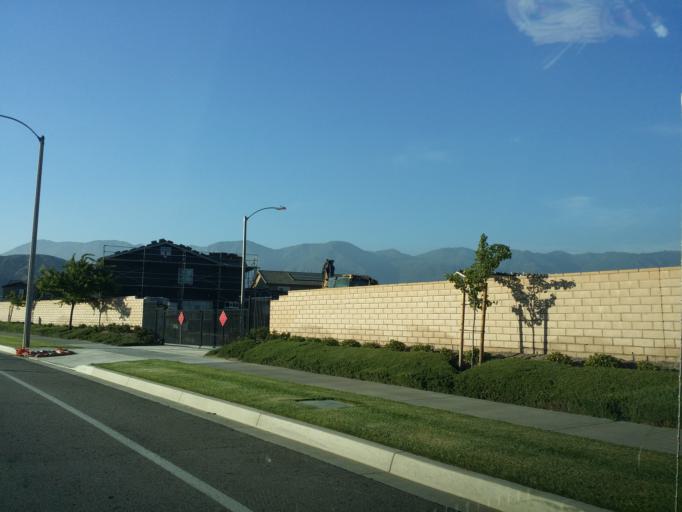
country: US
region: California
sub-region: San Bernardino County
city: Muscoy
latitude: 34.1904
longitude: -117.4176
